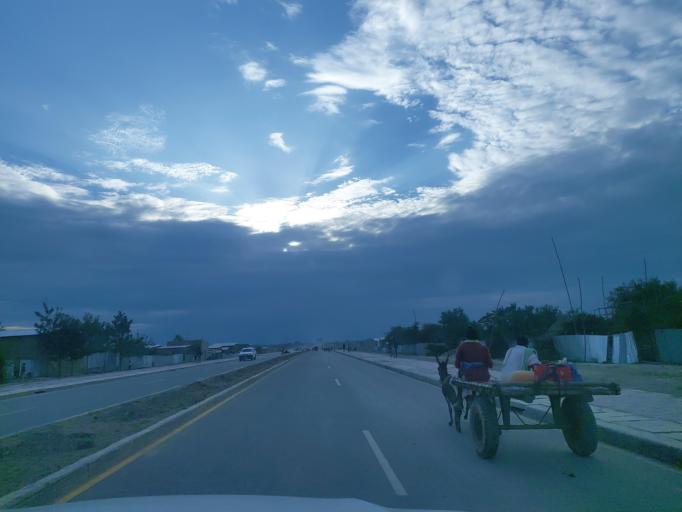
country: ET
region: Oromiya
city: Ziway
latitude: 8.1464
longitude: 38.8044
